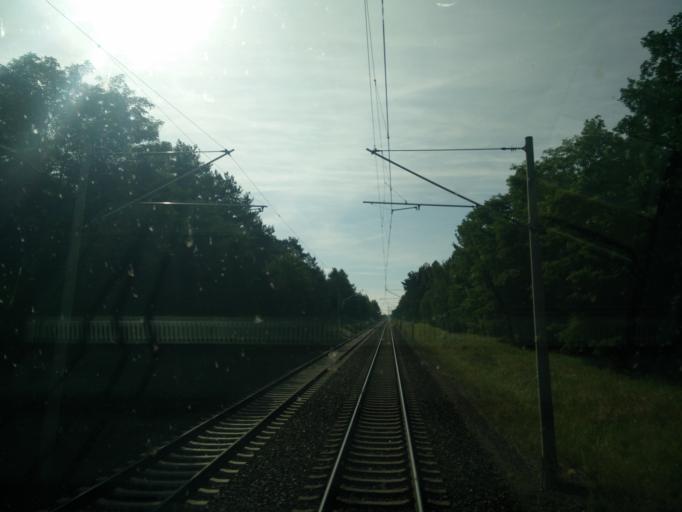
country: DE
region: Brandenburg
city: Kasel-Golzig
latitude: 51.9834
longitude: 13.7891
